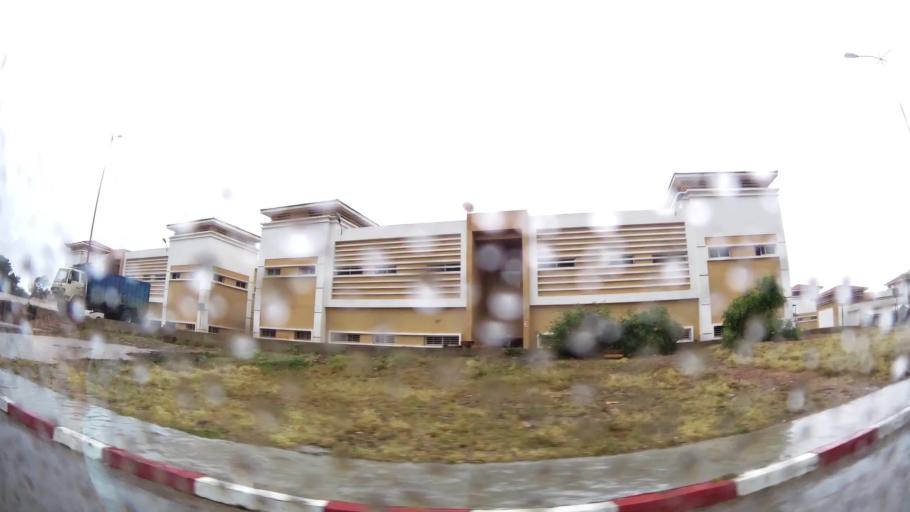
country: MA
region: Taza-Al Hoceima-Taounate
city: Al Hoceima
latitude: 35.2483
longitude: -3.9415
